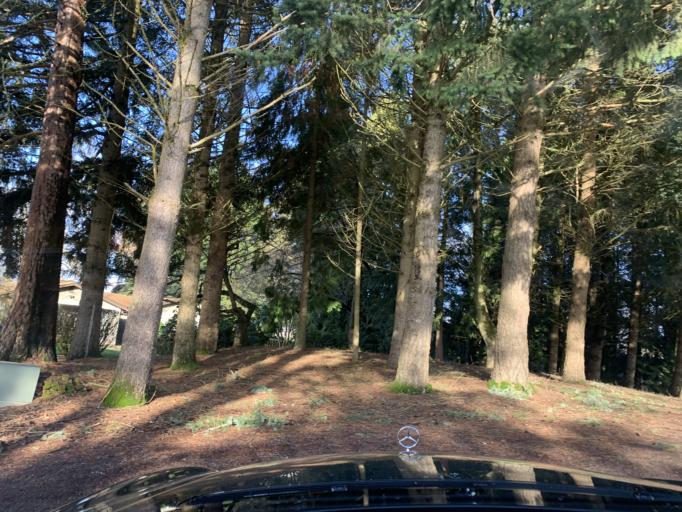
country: US
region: Washington
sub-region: Clark County
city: Five Corners
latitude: 45.7098
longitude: -122.5738
